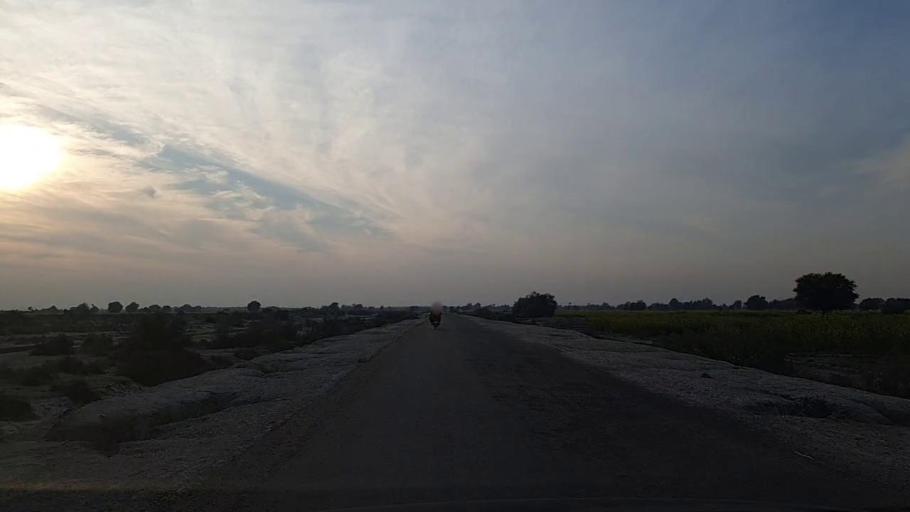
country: PK
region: Sindh
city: Jam Sahib
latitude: 26.4028
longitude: 68.4972
